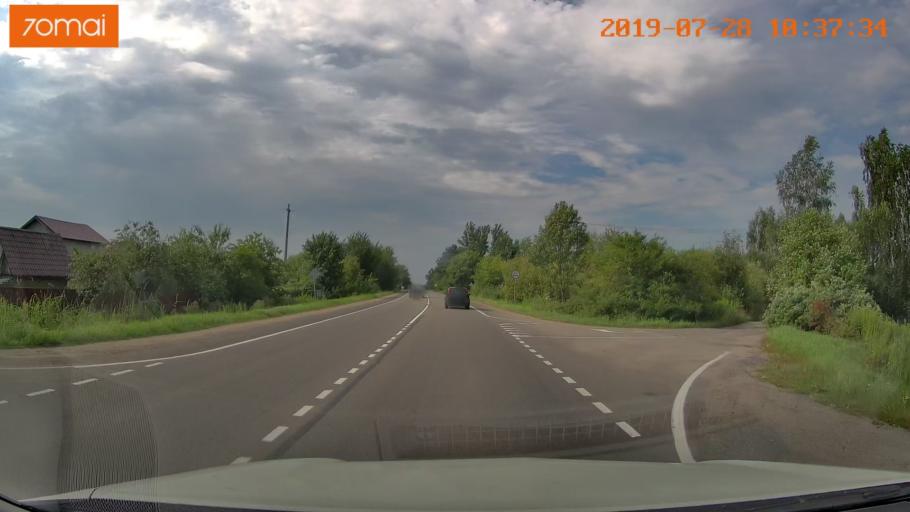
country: RU
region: Kaliningrad
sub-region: Gorod Kaliningrad
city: Kaliningrad
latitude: 54.7304
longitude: 20.4066
